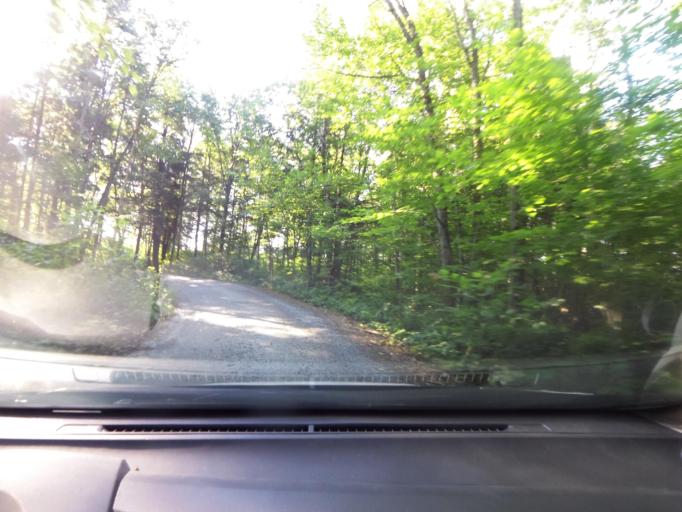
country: CA
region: Quebec
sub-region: Mauricie
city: Becancour
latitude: 46.5456
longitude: -72.4057
